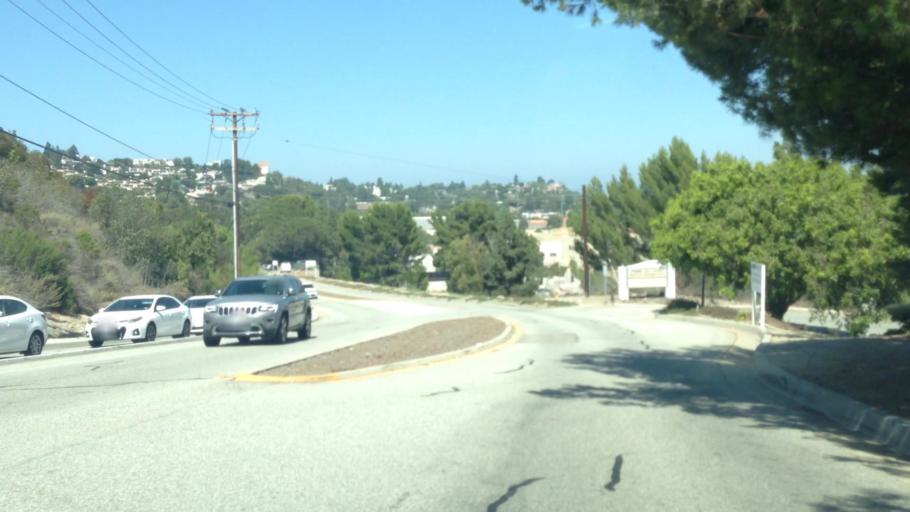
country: US
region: California
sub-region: Los Angeles County
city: Rolling Hills
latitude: 33.7688
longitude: -118.3709
